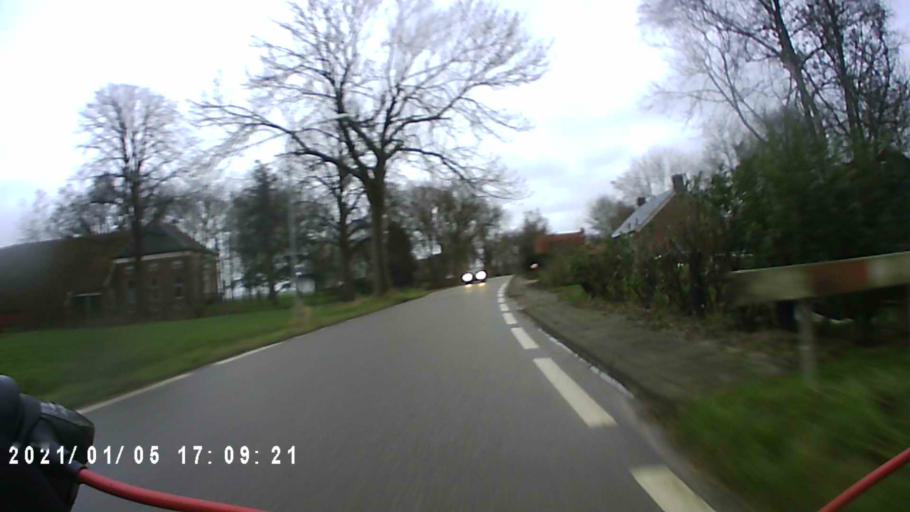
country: NL
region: Groningen
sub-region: Gemeente  Oldambt
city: Winschoten
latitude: 53.2487
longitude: 7.0093
